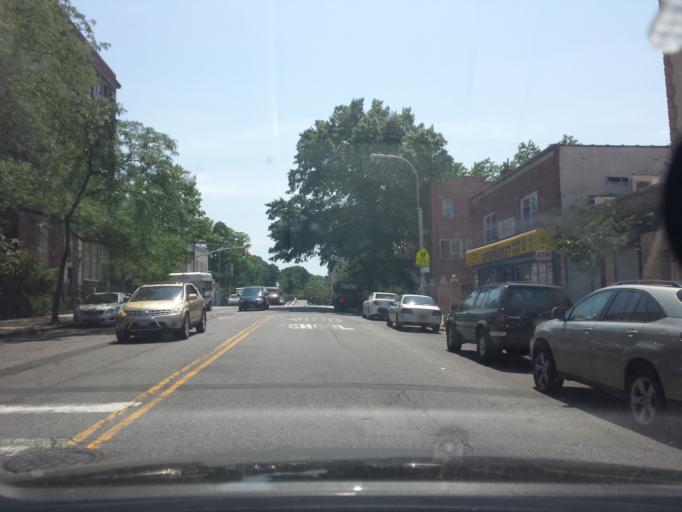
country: US
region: New York
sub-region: Kings County
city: Brooklyn
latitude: 40.6614
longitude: -73.9862
